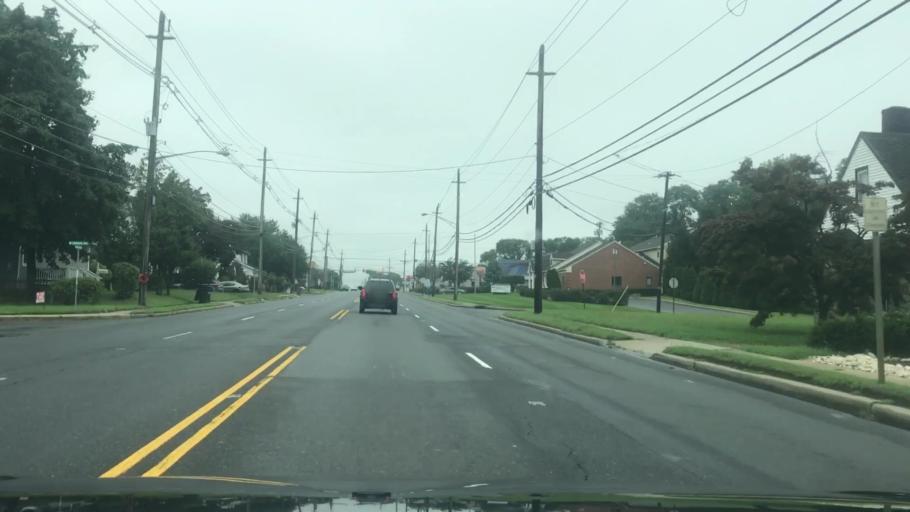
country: US
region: New Jersey
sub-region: Monmouth County
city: Red Bank
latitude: 40.3371
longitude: -74.0779
